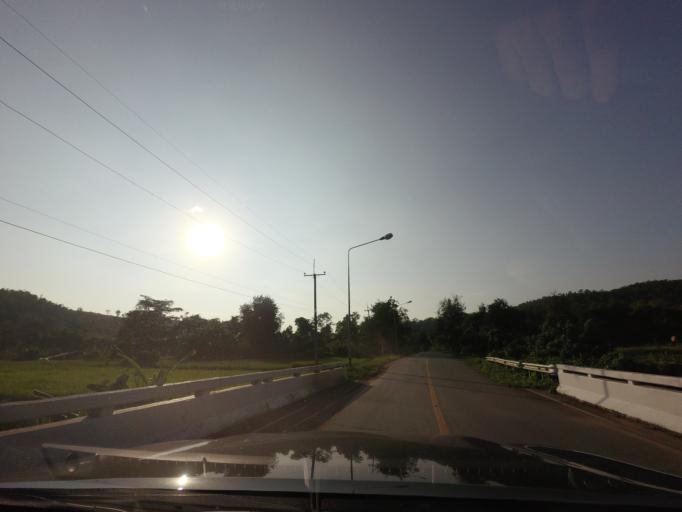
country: TH
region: Nan
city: Na Noi
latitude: 18.3353
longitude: 100.7848
